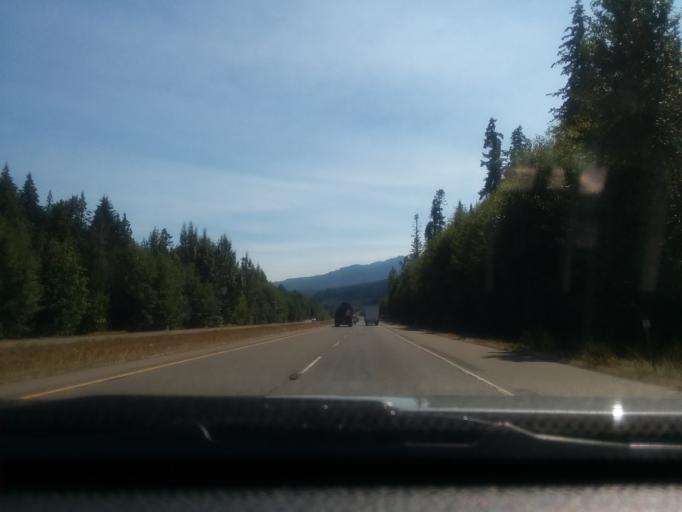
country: CA
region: British Columbia
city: Port Alberni
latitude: 49.4750
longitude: -124.8061
